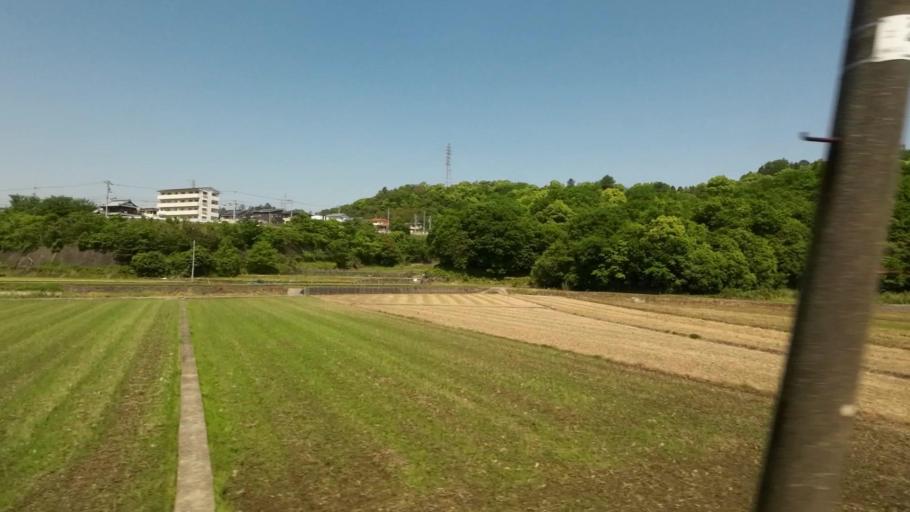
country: JP
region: Ehime
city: Niihama
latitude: 33.9323
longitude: 133.2717
